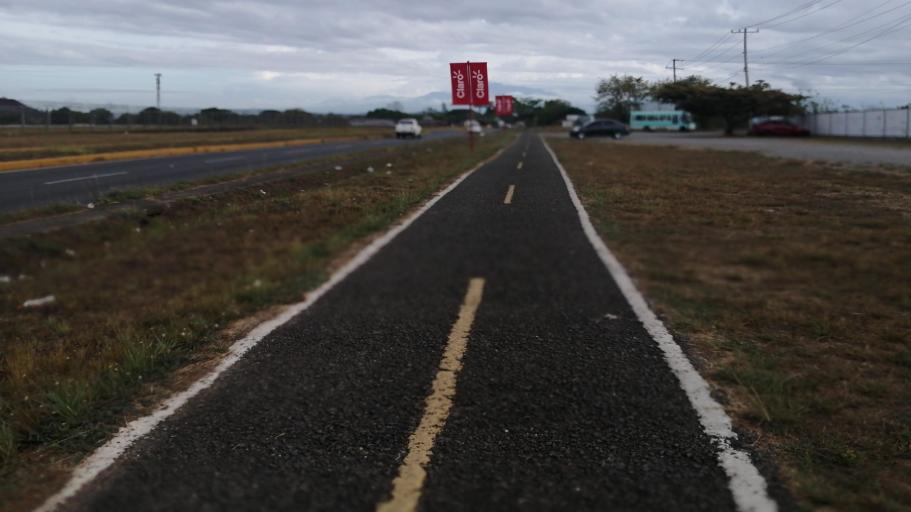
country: PA
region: Chiriqui
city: David
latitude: 8.3971
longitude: -82.4280
